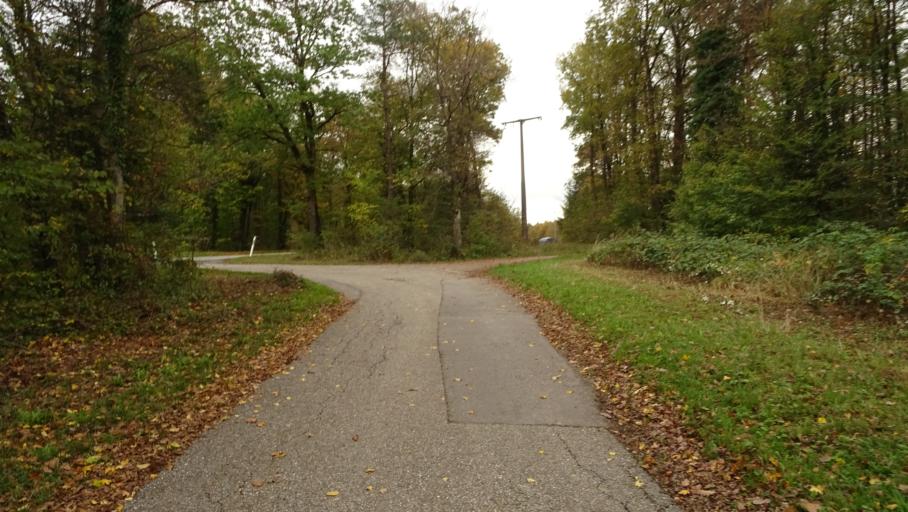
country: DE
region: Baden-Wuerttemberg
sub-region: Karlsruhe Region
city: Obrigheim
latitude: 49.3848
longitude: 9.1026
